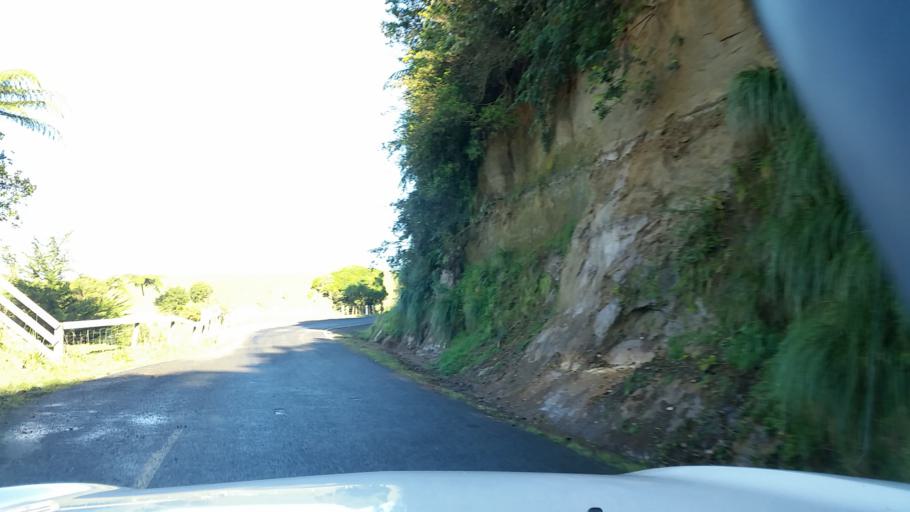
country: NZ
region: Taranaki
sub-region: South Taranaki District
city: Eltham
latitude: -39.5152
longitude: 174.3815
